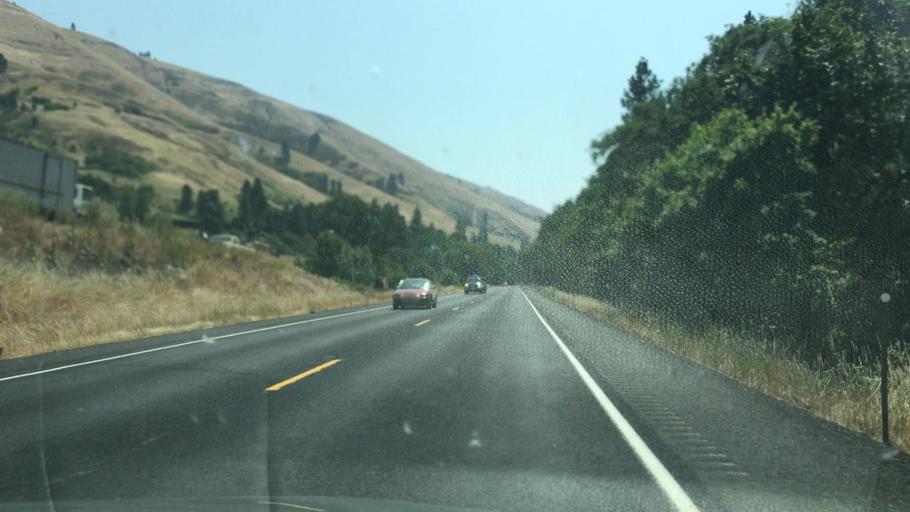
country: US
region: Idaho
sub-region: Nez Perce County
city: Lapwai
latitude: 46.3625
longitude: -116.6370
